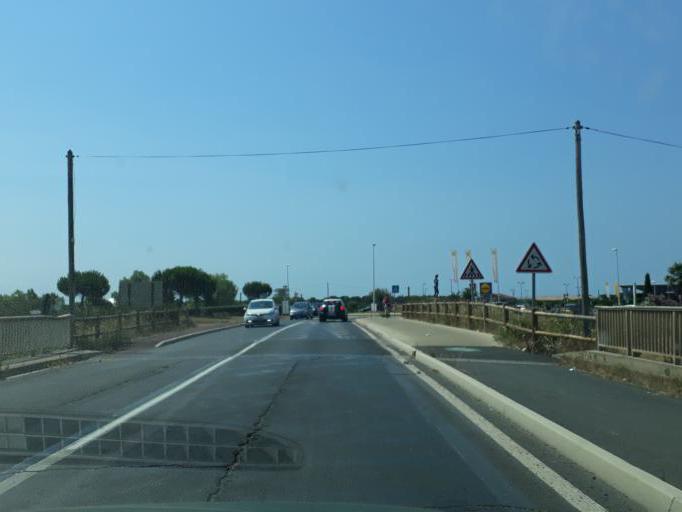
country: FR
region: Languedoc-Roussillon
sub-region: Departement de l'Herault
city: Agde
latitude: 43.2974
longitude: 3.4708
